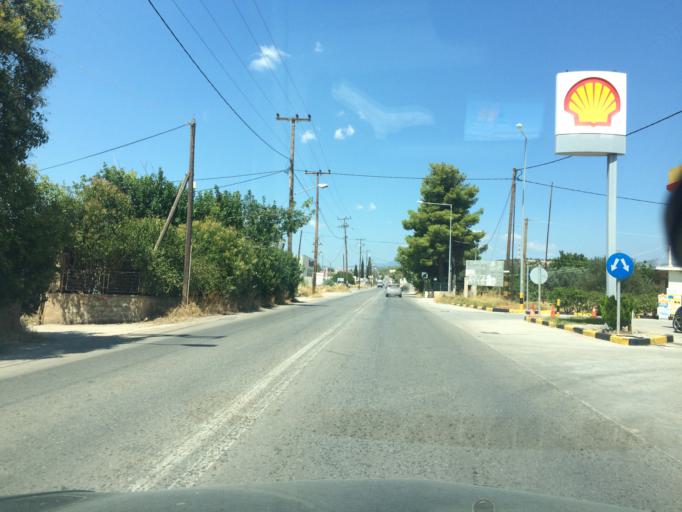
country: GR
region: Central Greece
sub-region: Nomos Evvoias
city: Nea Artaki
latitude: 38.5196
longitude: 23.6373
